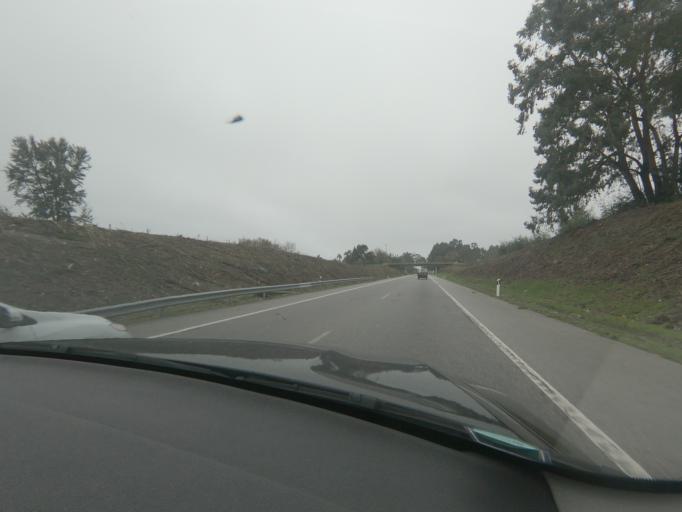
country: PT
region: Viseu
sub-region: Concelho de Tondela
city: Tondela
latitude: 40.5731
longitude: -8.0336
